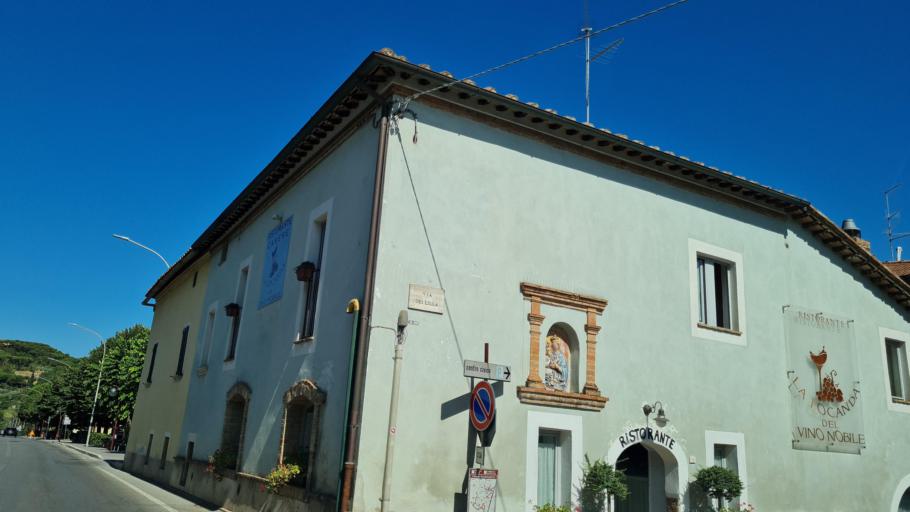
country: IT
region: Tuscany
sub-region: Provincia di Siena
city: Sant'Albino
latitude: 43.0715
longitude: 11.8056
